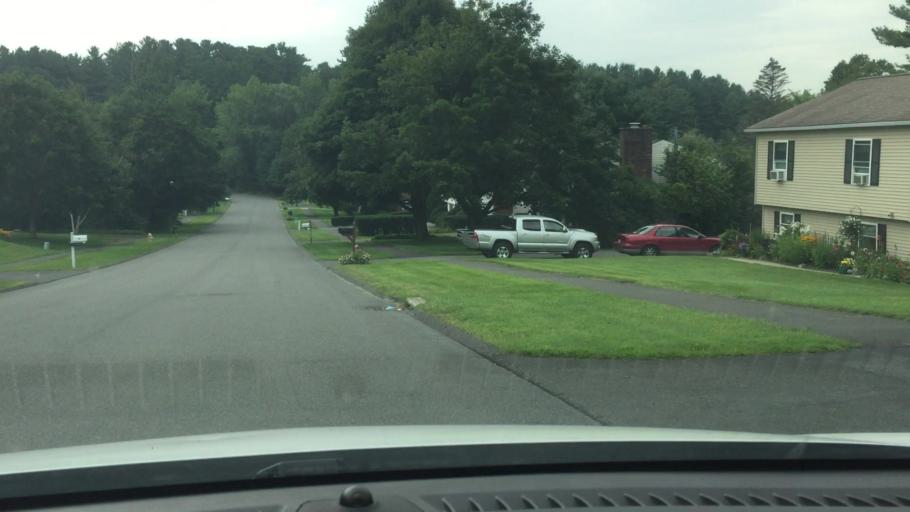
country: US
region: Massachusetts
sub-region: Berkshire County
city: Pittsfield
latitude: 42.4516
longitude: -73.2813
